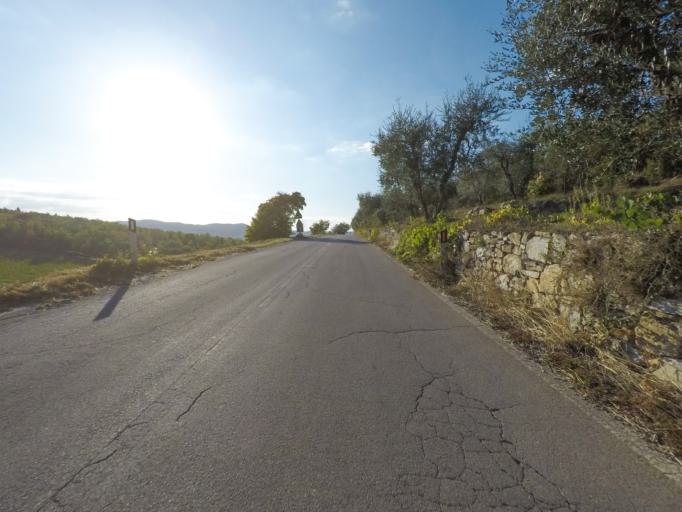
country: IT
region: Tuscany
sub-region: Provincia di Siena
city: Radda in Chianti
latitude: 43.4518
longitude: 11.3887
